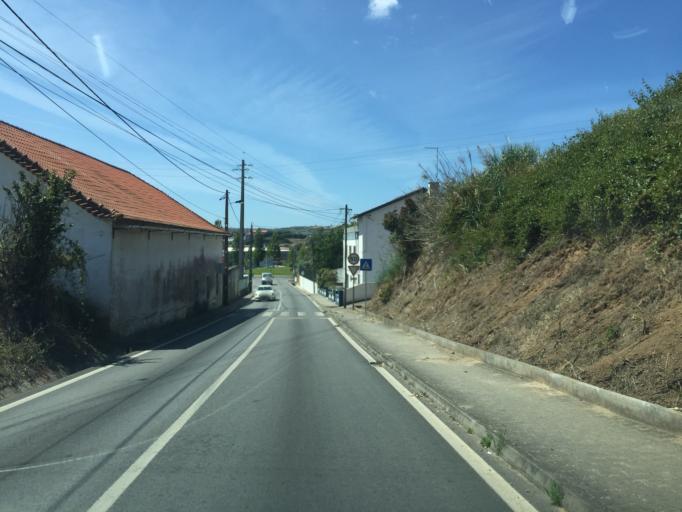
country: PT
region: Lisbon
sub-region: Lourinha
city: Lourinha
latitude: 39.2522
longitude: -9.3134
